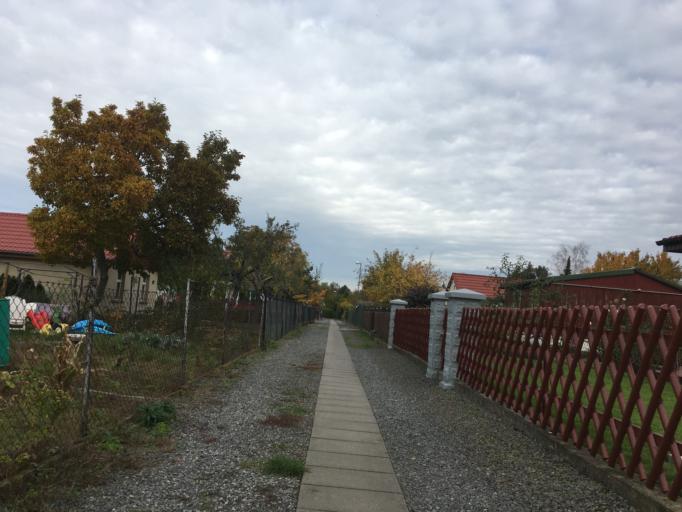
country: DE
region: Berlin
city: Weissensee
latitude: 52.5674
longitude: 13.4602
